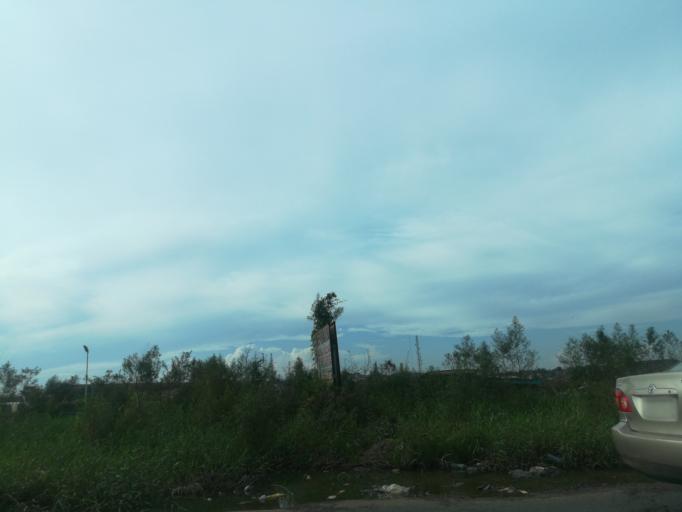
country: NG
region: Oyo
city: Ibadan
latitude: 7.4002
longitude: 3.9404
